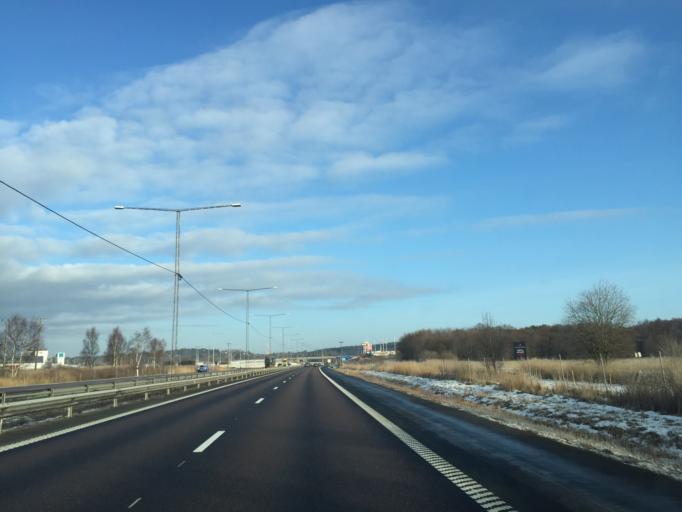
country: SE
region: Vaestra Goetaland
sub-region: Stenungsunds Kommun
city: Stora Hoga
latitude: 58.0194
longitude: 11.8442
